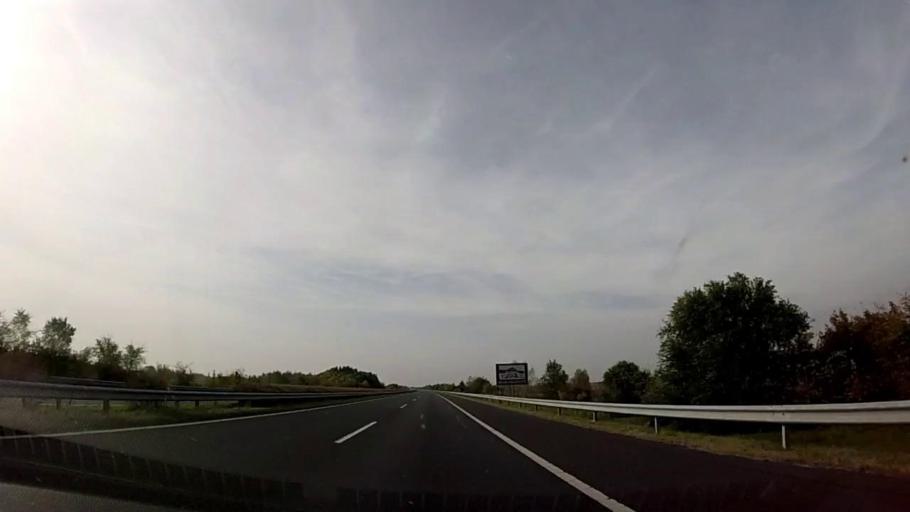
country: HU
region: Somogy
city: Fonyod
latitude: 46.7423
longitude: 17.6083
